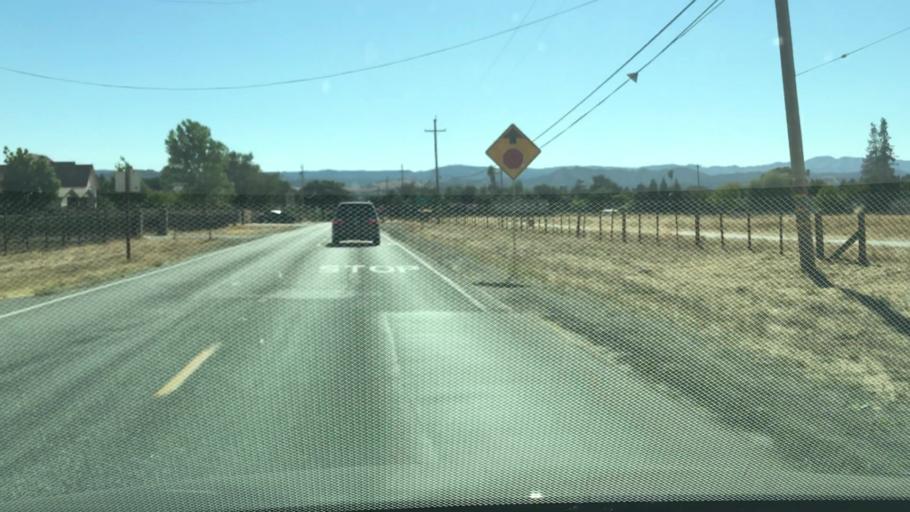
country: US
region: California
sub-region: Santa Clara County
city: San Martin
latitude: 37.0958
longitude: -121.5797
